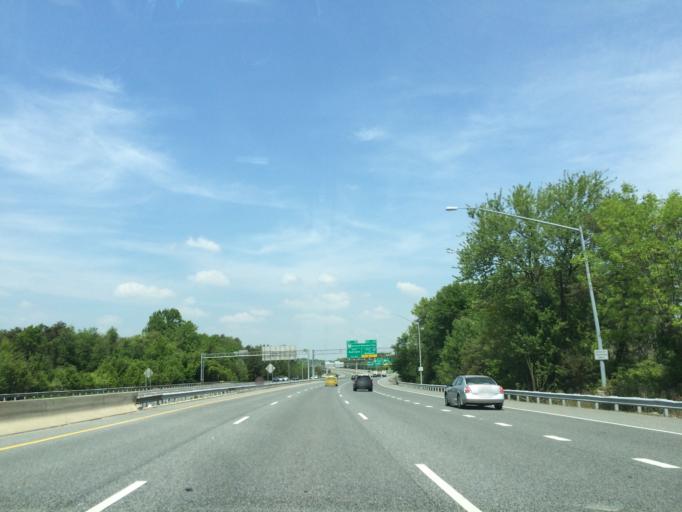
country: US
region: Maryland
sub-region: Howard County
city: Elkridge
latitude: 39.1914
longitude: -76.6867
